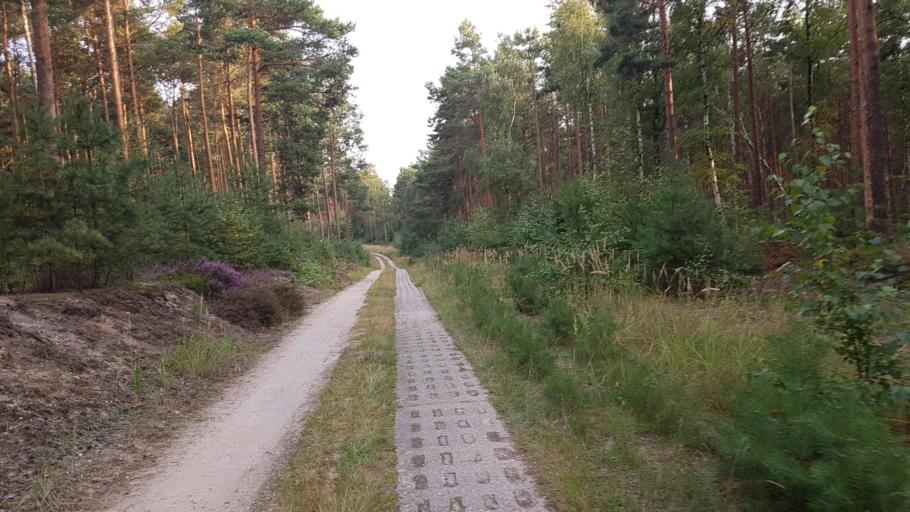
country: DE
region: Brandenburg
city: Schonborn
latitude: 51.6338
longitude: 13.4979
